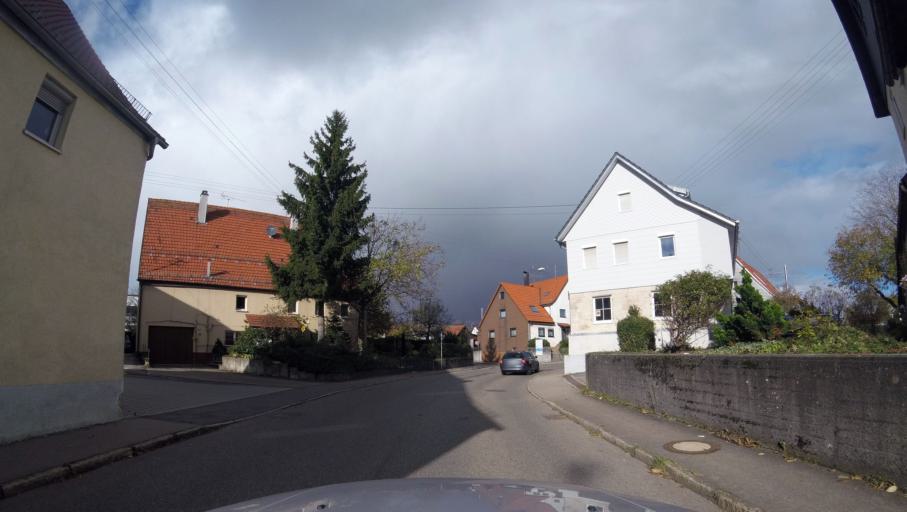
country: DE
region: Baden-Wuerttemberg
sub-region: Regierungsbezirk Stuttgart
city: Mutlangen
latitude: 48.8130
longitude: 9.7534
